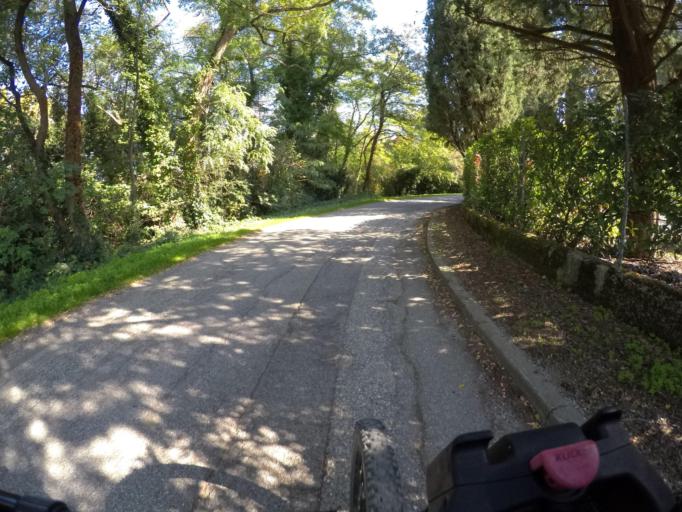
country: IT
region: Friuli Venezia Giulia
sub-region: Provincia di Udine
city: Buttrio
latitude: 46.0136
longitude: 13.3605
